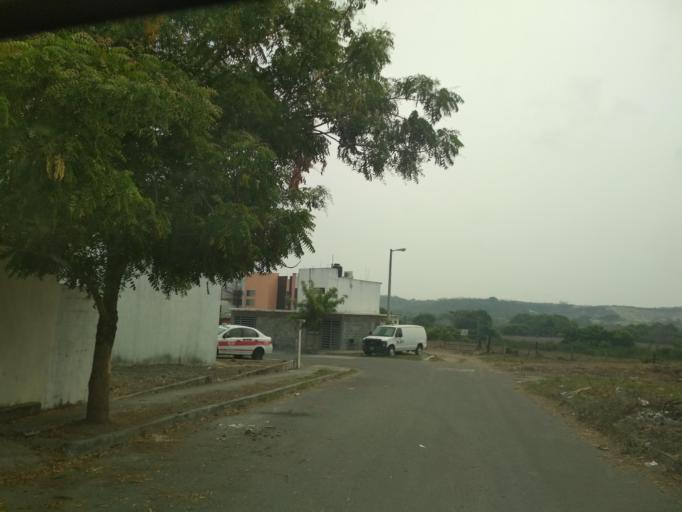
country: MX
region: Veracruz
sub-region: Veracruz
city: Fraccionamiento Geovillas los Pinos
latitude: 19.2309
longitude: -96.2413
